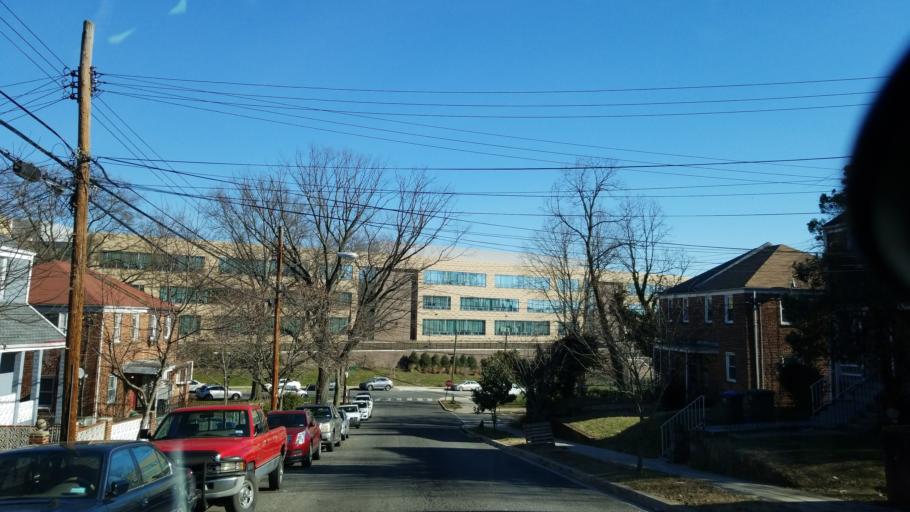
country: US
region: Maryland
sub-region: Prince George's County
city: Glassmanor
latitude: 38.8380
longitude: -77.0036
